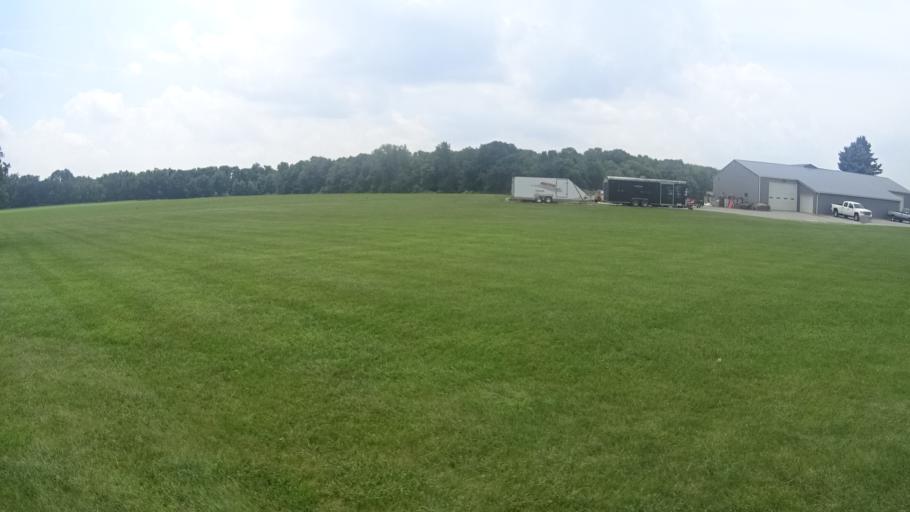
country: US
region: Ohio
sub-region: Erie County
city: Milan
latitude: 41.3084
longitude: -82.6610
